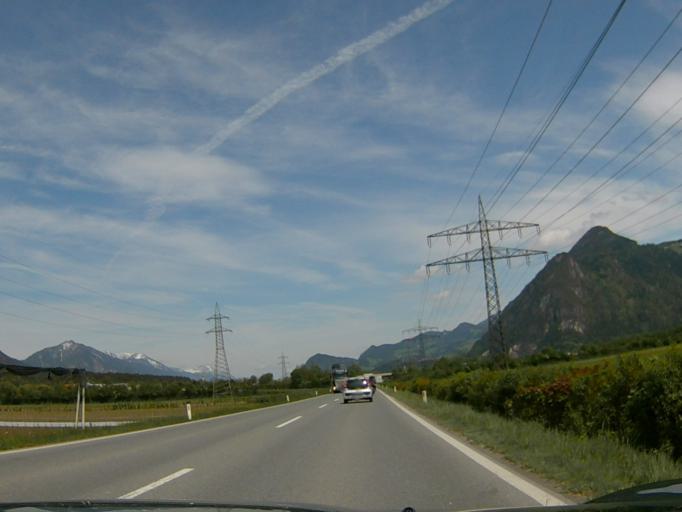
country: AT
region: Tyrol
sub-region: Politischer Bezirk Schwaz
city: Wiesing
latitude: 47.3957
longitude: 11.8016
